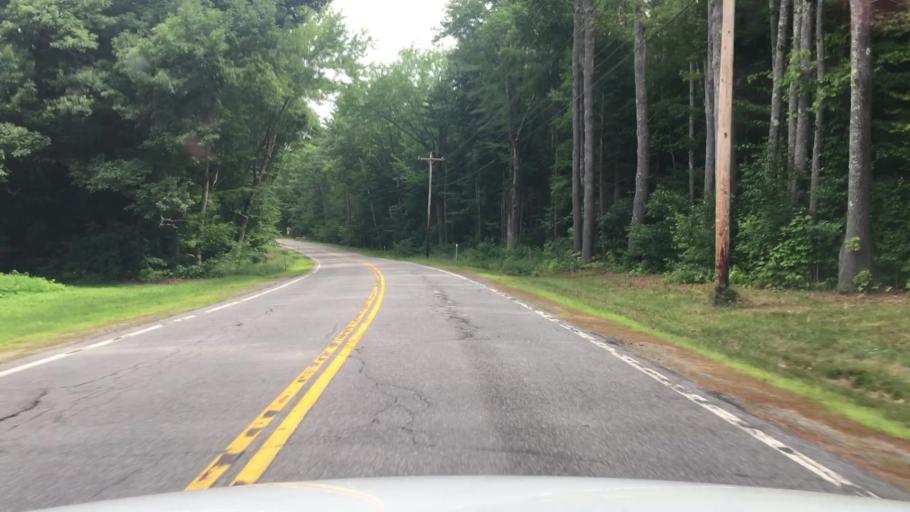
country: US
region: New Hampshire
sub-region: Grafton County
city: Plymouth
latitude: 43.7782
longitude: -71.6682
